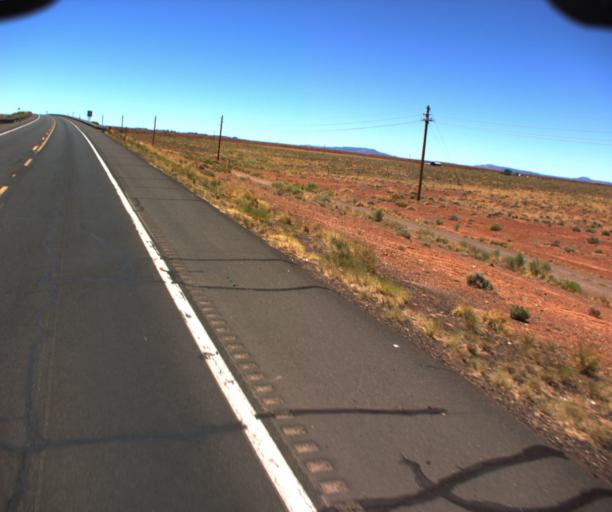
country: US
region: Arizona
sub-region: Navajo County
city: Winslow
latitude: 35.0141
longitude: -110.7021
